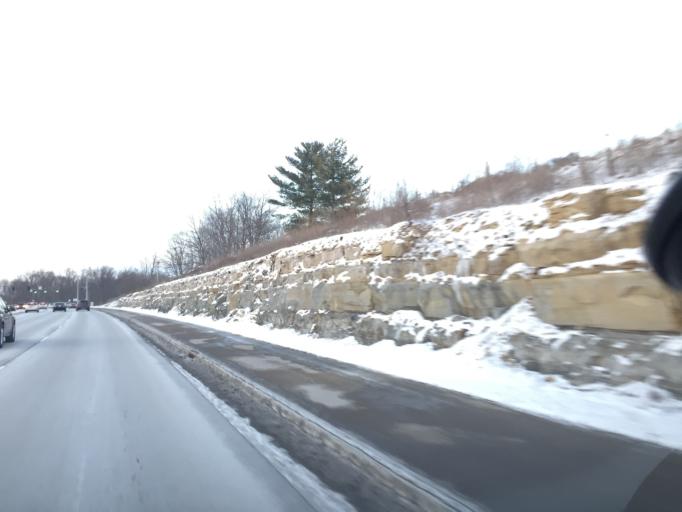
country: US
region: Indiana
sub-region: Monroe County
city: Bloomington
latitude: 39.1781
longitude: -86.5059
